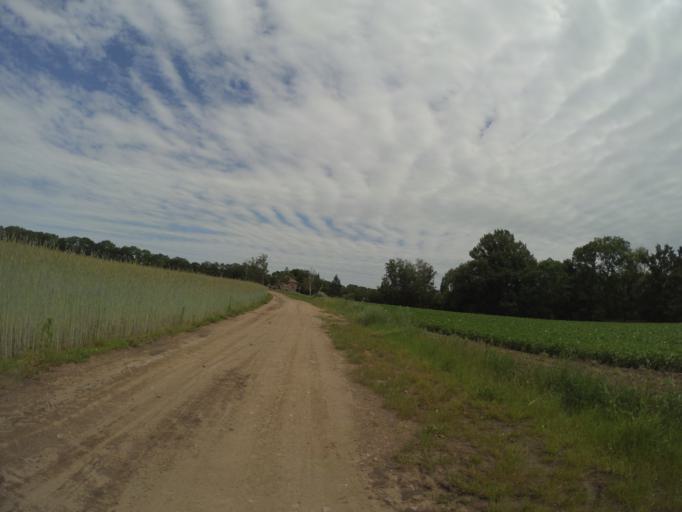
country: CZ
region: Central Bohemia
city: Prerov nad Labem
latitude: 50.1820
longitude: 14.8047
